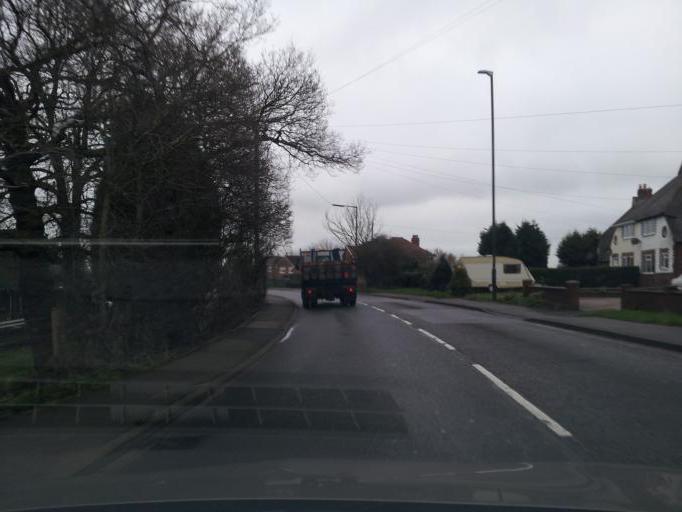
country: GB
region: England
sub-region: Derbyshire
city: Swadlincote
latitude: 52.7854
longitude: -1.5552
